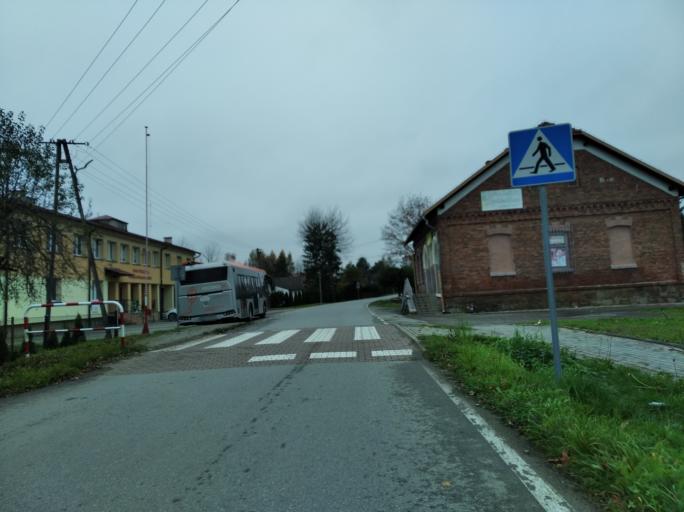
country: PL
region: Subcarpathian Voivodeship
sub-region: Powiat krosnienski
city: Leki
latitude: 49.8055
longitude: 21.6634
